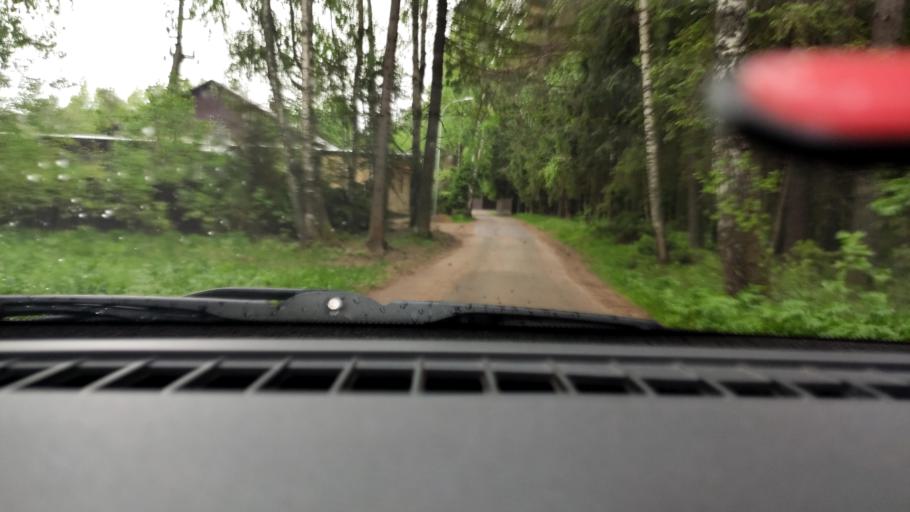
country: RU
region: Perm
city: Karagay
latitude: 58.2376
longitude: 54.8727
